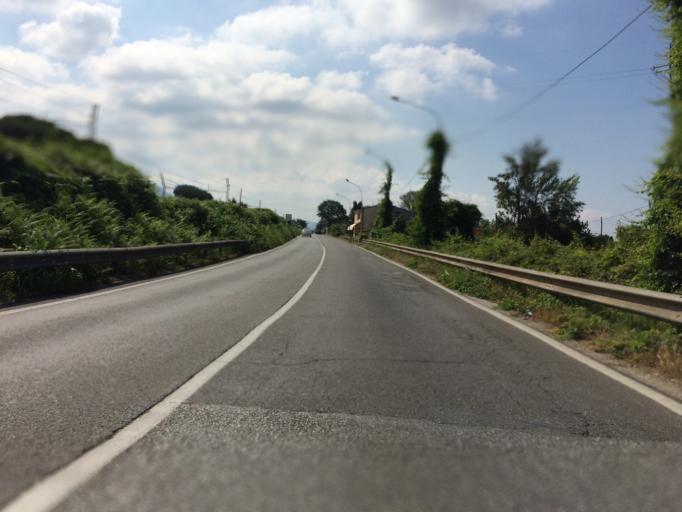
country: IT
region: Tuscany
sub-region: Provincia di Lucca
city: Strettoia
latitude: 43.9892
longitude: 10.1833
